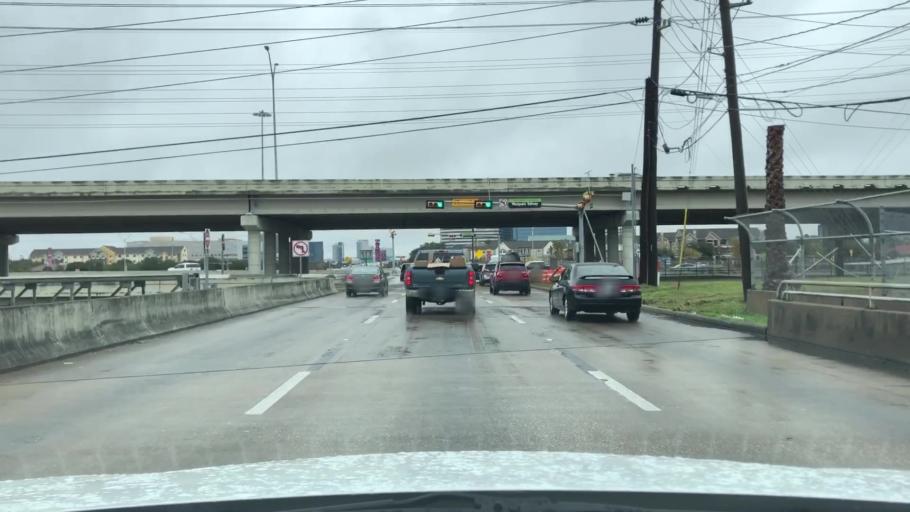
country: US
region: Texas
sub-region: Harris County
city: Bunker Hill Village
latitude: 29.7176
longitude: -95.5565
